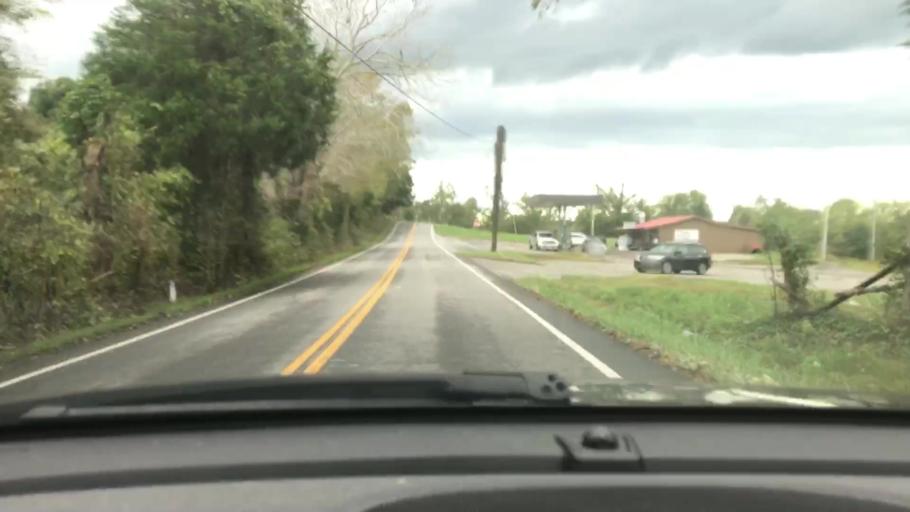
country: US
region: Tennessee
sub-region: Cheatham County
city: Ashland City
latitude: 36.2691
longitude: -87.2074
